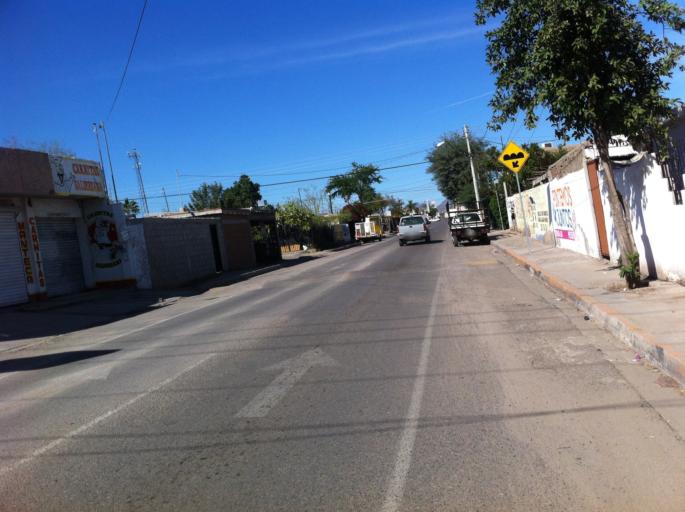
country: MX
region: Sonora
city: Hermosillo
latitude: 29.1077
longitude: -111.0113
